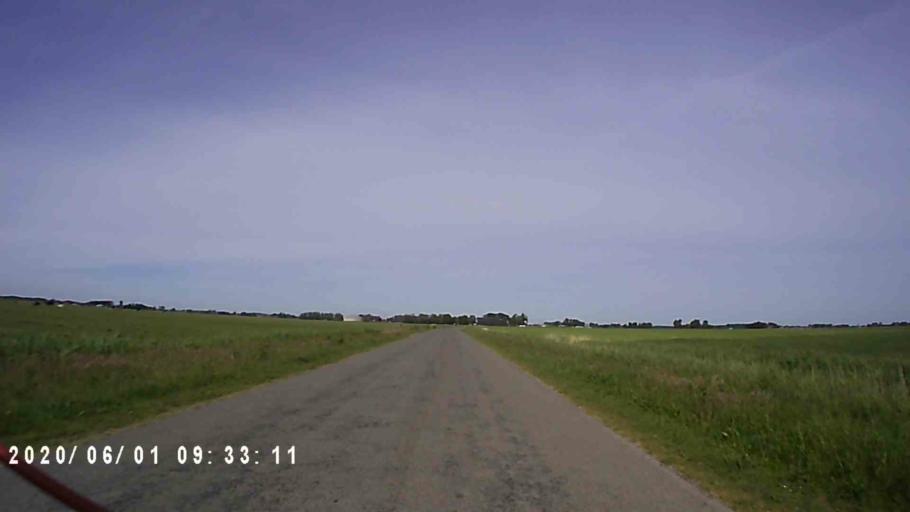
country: NL
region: Friesland
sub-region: Gemeente Leeuwarderadeel
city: Stiens
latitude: 53.2621
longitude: 5.7232
